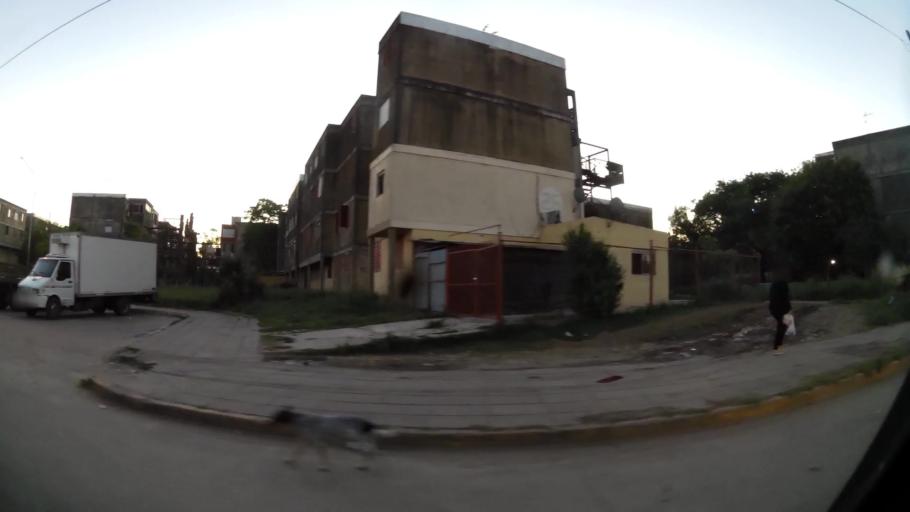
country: AR
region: Buenos Aires
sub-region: Partido de Almirante Brown
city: Adrogue
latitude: -34.7905
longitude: -58.3222
